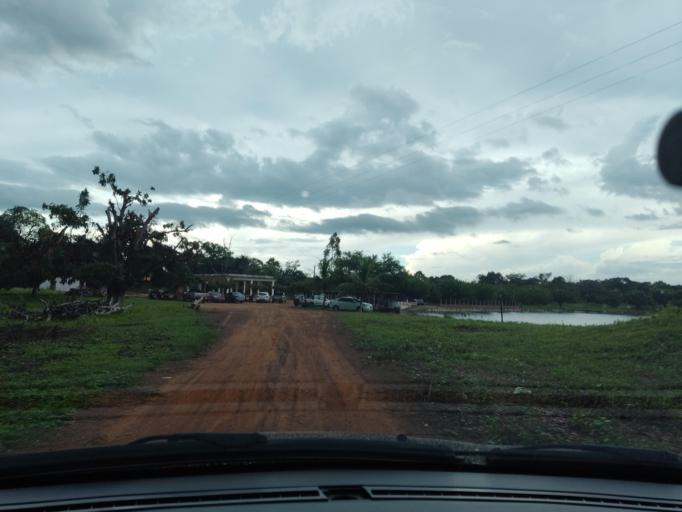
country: BR
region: Piaui
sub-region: Valenca Do Piaui
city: Valenca do Piaui
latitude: -6.3534
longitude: -41.7072
